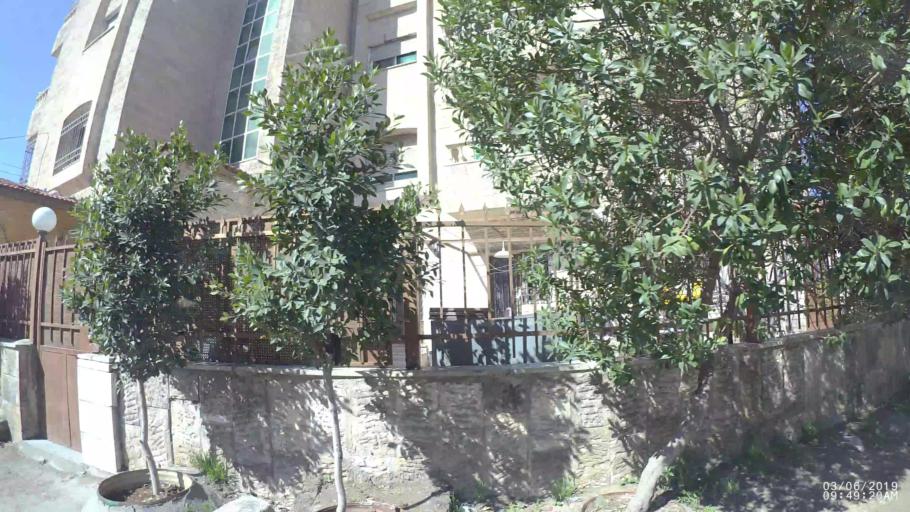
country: JO
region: Amman
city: Amman
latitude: 31.9915
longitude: 35.9830
